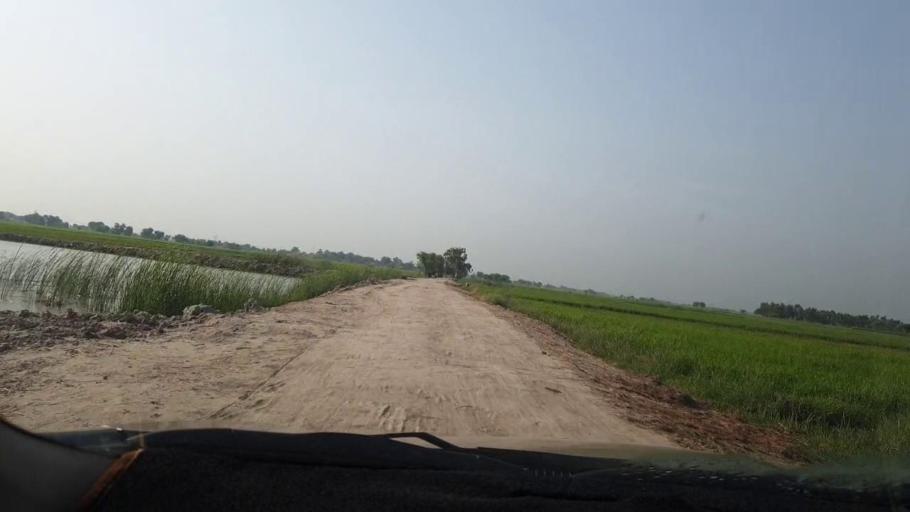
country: PK
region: Sindh
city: Goth Garelo
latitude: 27.4710
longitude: 68.0883
